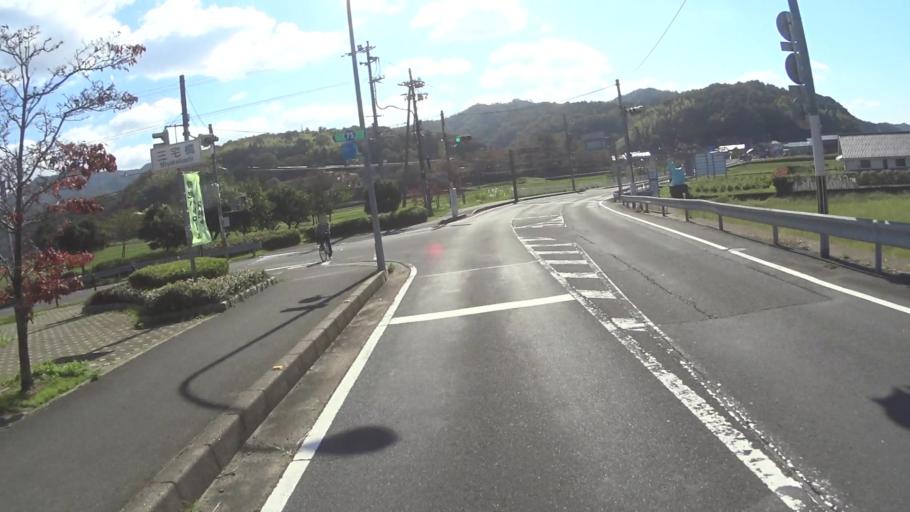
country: JP
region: Kyoto
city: Miyazu
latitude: 35.7139
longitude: 135.1058
